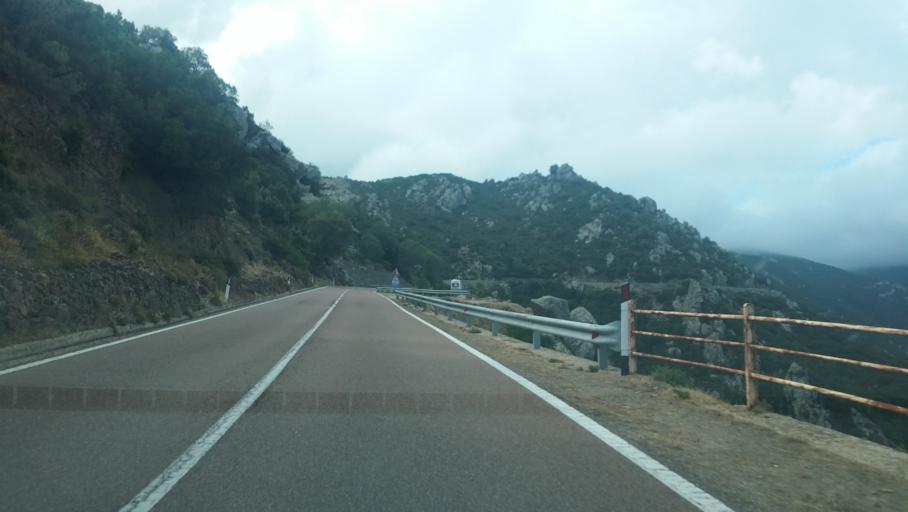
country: IT
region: Sardinia
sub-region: Provincia di Ogliastra
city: Urzulei
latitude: 40.1836
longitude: 9.5332
